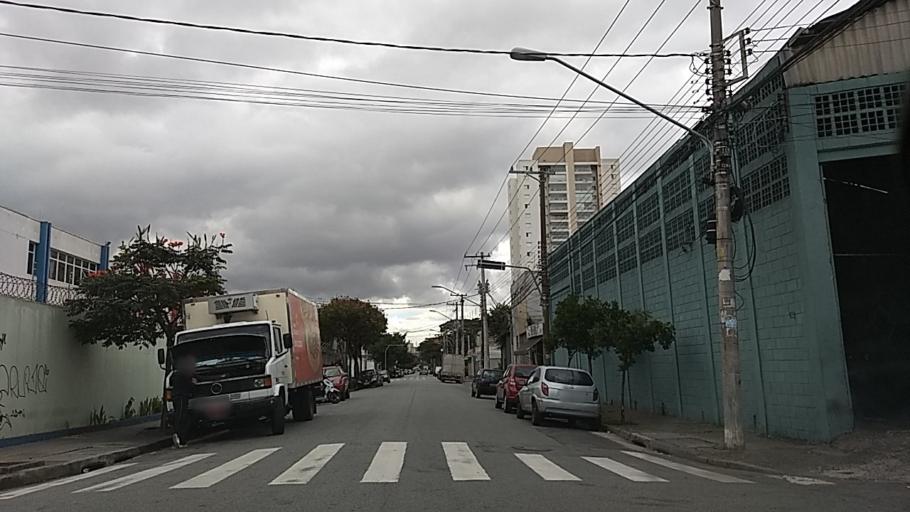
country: BR
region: Sao Paulo
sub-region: Sao Paulo
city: Sao Paulo
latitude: -23.5183
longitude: -46.6119
